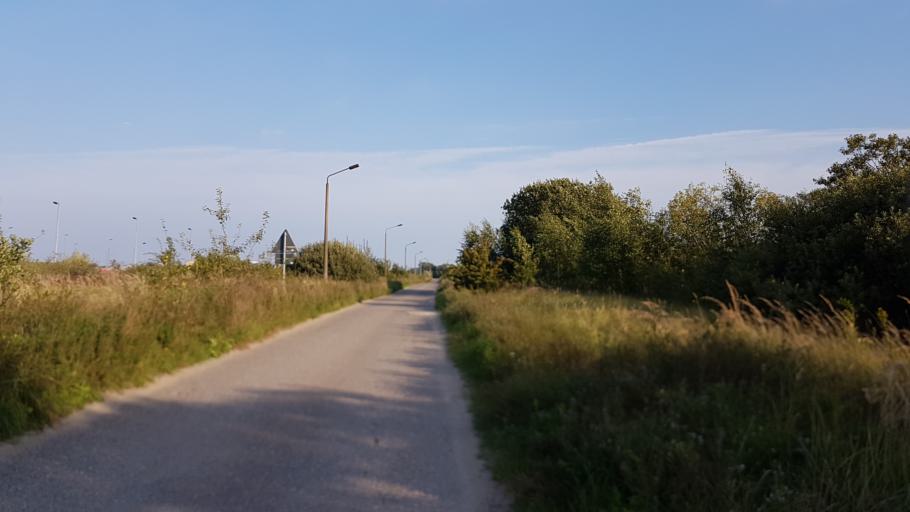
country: DE
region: Mecklenburg-Vorpommern
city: Sagard
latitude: 54.5011
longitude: 13.5377
